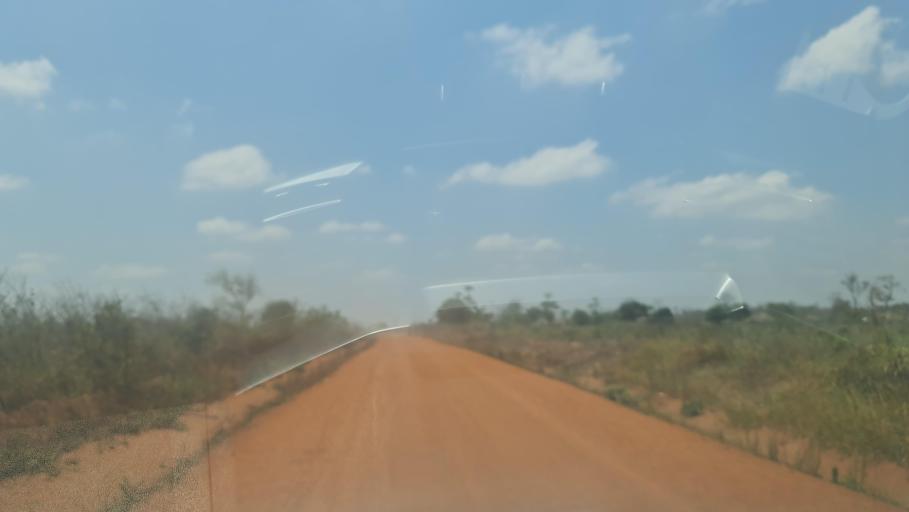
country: MW
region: Southern Region
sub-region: Nsanje District
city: Nsanje
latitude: -17.3389
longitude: 35.7218
